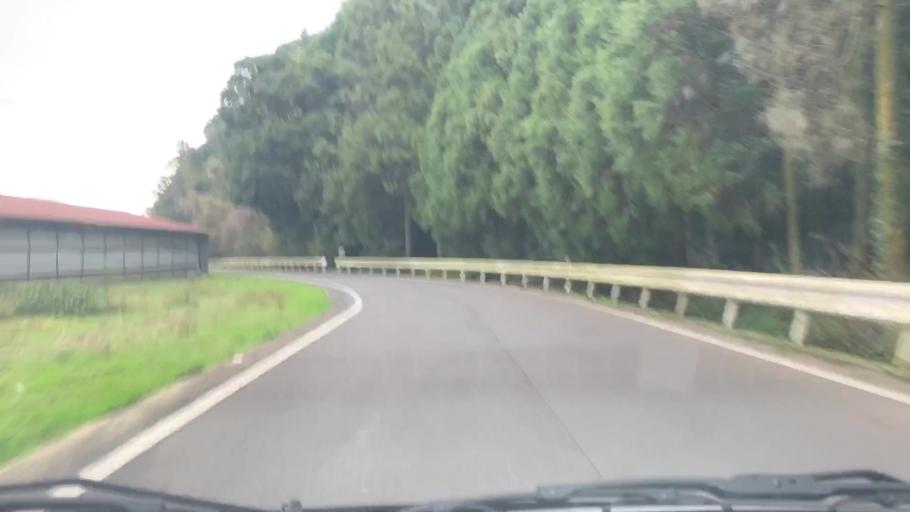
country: JP
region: Saga Prefecture
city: Ureshinomachi-shimojuku
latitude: 33.1236
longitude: 130.0475
